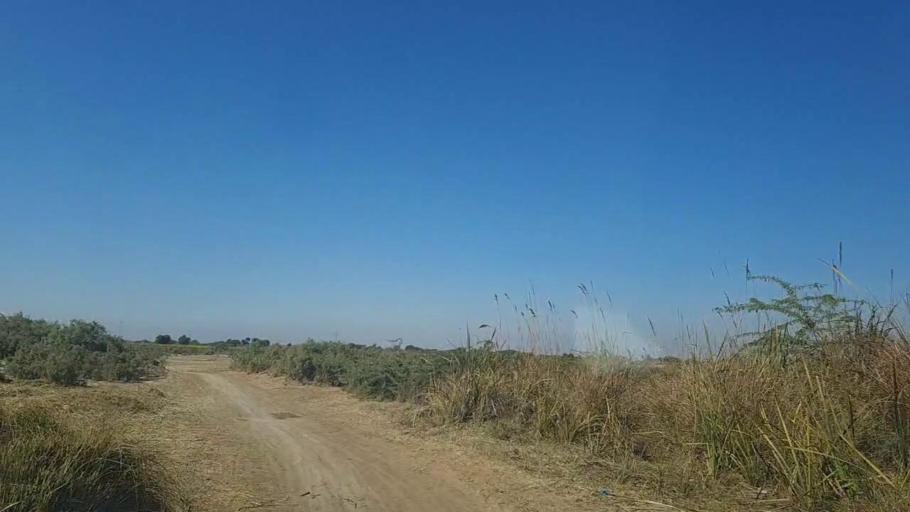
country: PK
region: Sindh
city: Khadro
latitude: 26.1574
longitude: 68.8234
